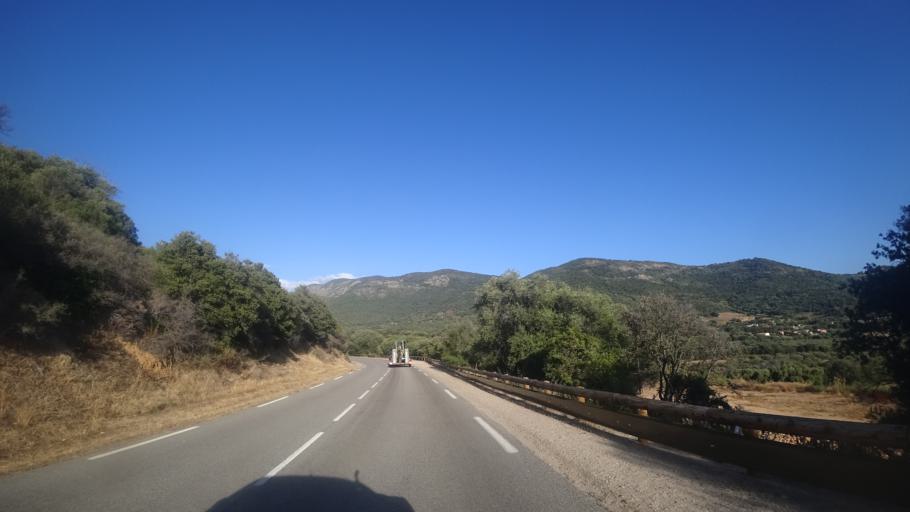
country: FR
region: Corsica
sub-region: Departement de la Corse-du-Sud
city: Cargese
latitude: 42.1581
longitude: 8.6017
